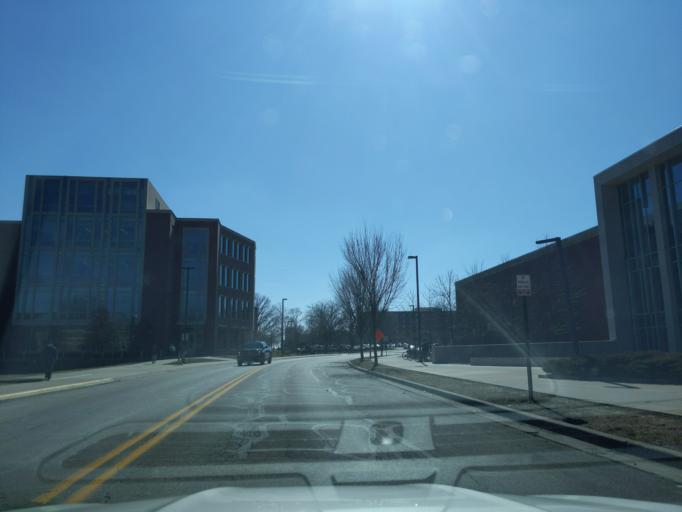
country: US
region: Indiana
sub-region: Tippecanoe County
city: West Lafayette
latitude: 40.4285
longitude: -86.9217
